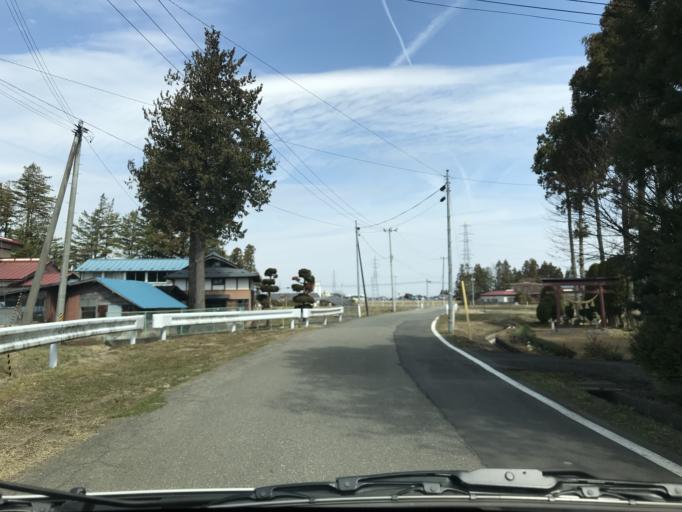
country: JP
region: Iwate
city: Mizusawa
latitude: 39.1329
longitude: 141.0834
